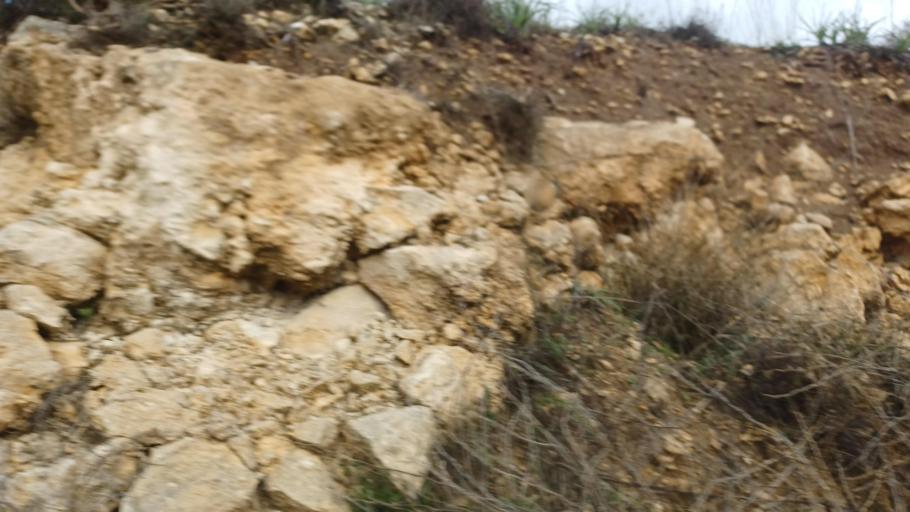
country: CY
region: Limassol
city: Pachna
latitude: 34.8239
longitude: 32.7349
